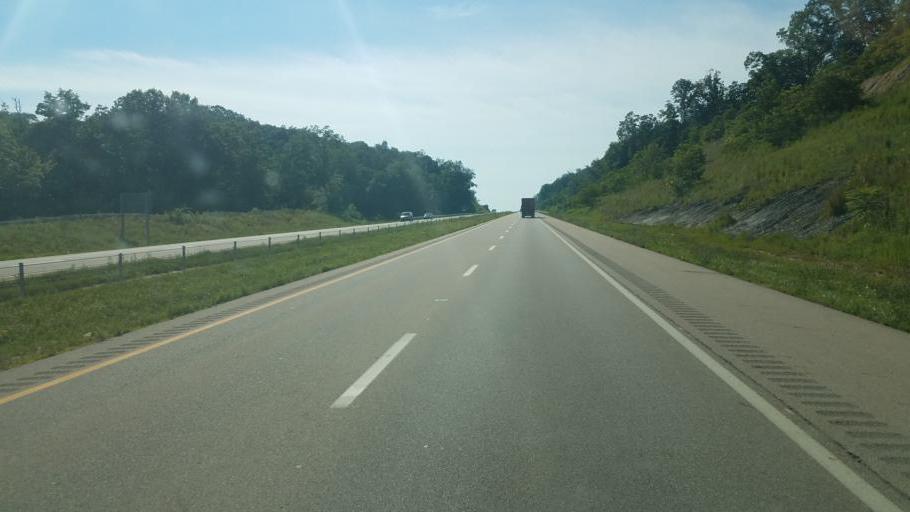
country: US
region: Ohio
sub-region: Athens County
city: Nelsonville
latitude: 39.4713
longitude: -82.2710
